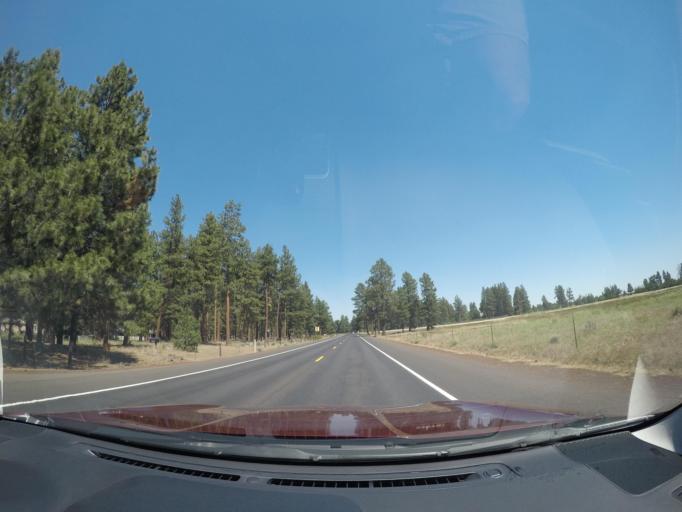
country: US
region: Oregon
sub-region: Deschutes County
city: Sisters
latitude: 44.2878
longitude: -121.5292
